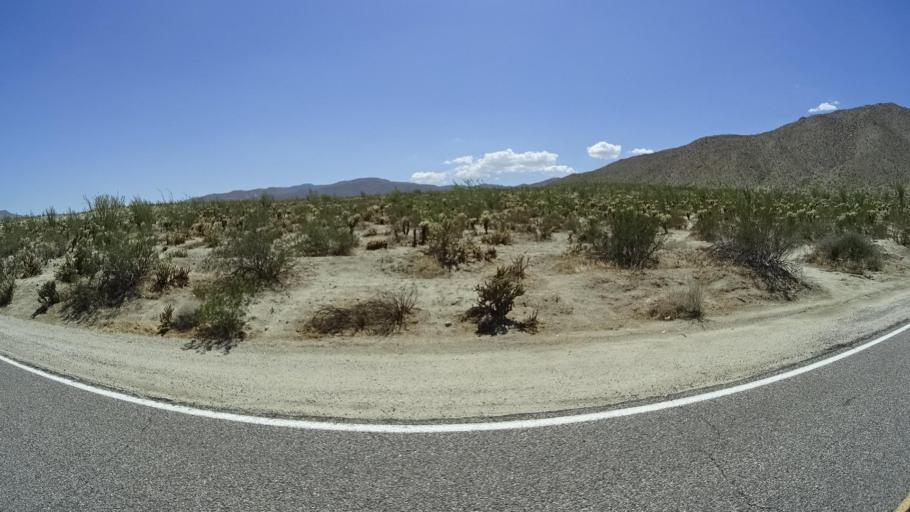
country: US
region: California
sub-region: San Diego County
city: Borrego Springs
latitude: 33.1340
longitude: -116.3630
